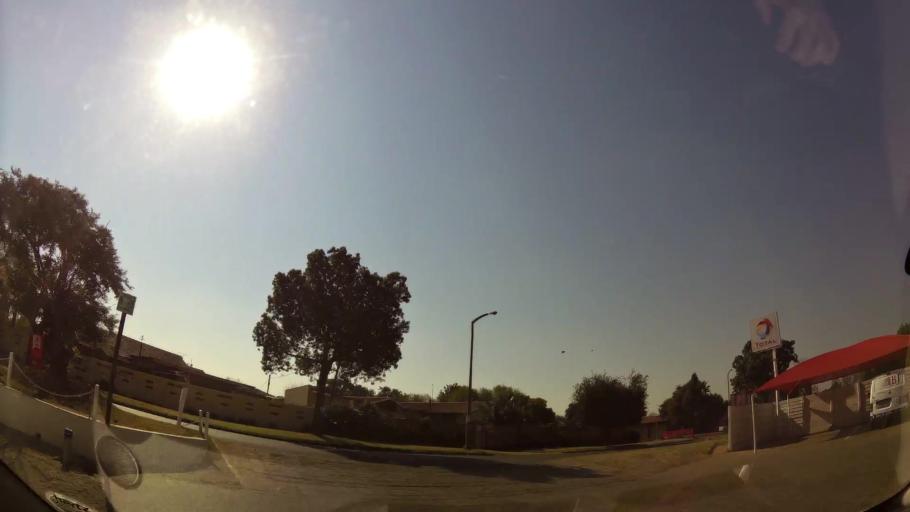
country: ZA
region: Gauteng
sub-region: Ekurhuleni Metropolitan Municipality
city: Boksburg
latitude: -26.1660
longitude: 28.2583
